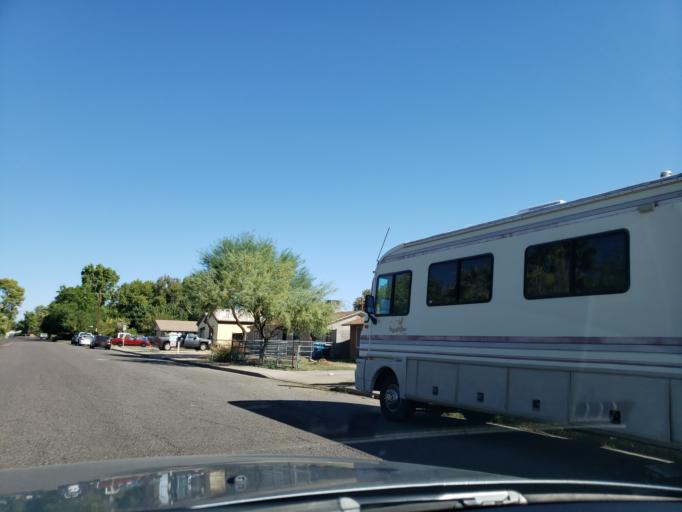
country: US
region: Arizona
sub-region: Maricopa County
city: Glendale
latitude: 33.4831
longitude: -112.1595
